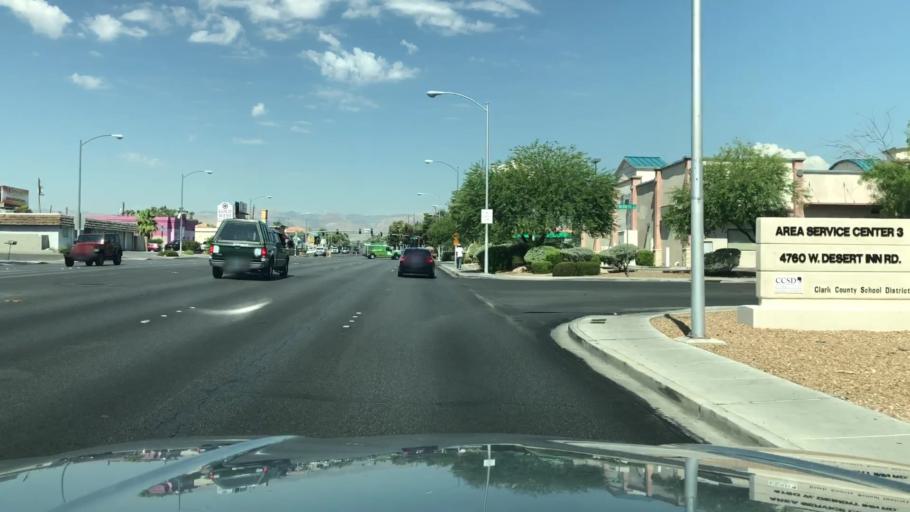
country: US
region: Nevada
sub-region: Clark County
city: Spring Valley
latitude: 36.1301
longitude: -115.2054
